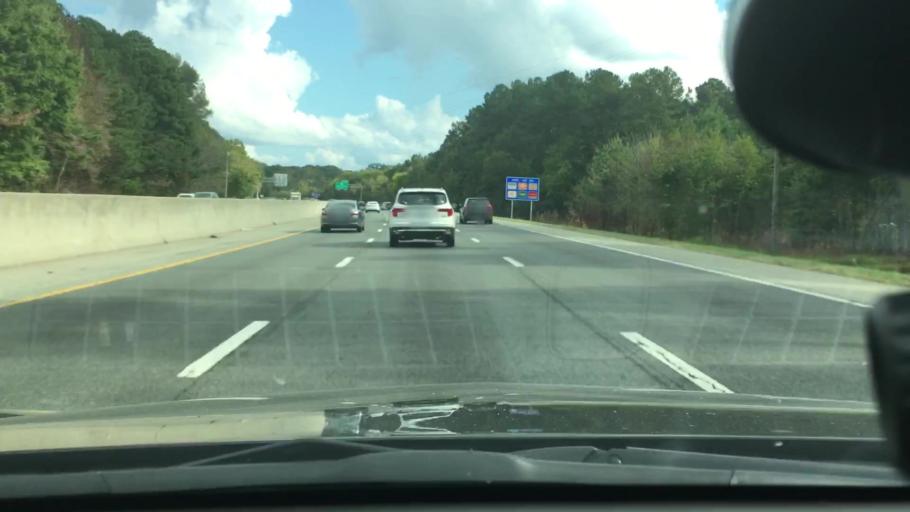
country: US
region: North Carolina
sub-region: Orange County
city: Chapel Hill
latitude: 35.9072
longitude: -78.9761
